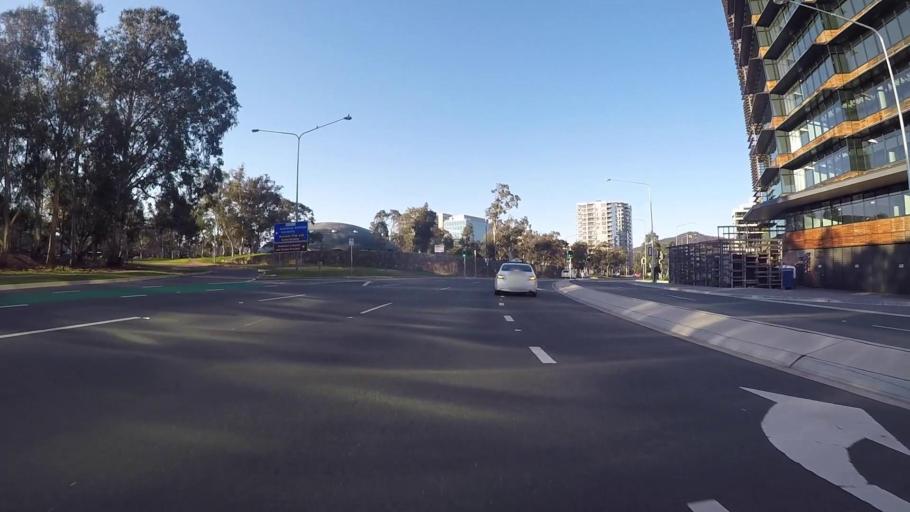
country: AU
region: Australian Capital Territory
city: Canberra
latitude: -35.2848
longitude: 149.1223
